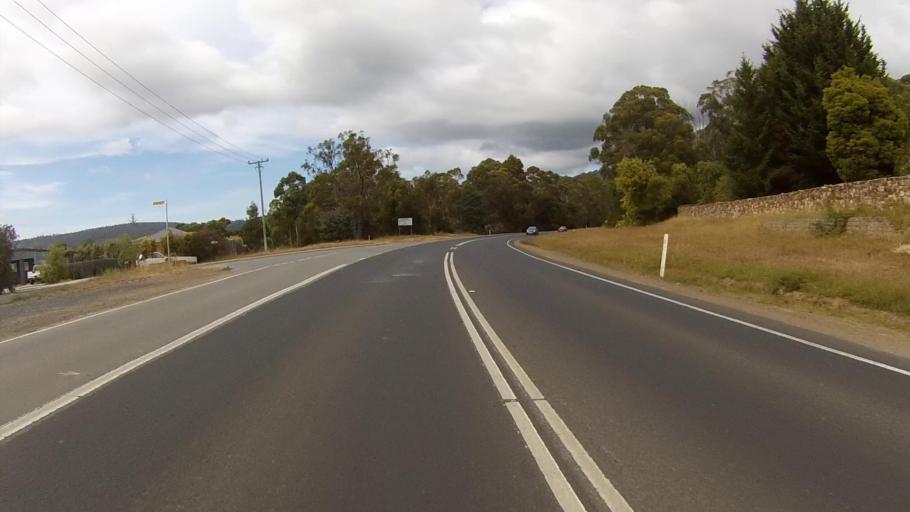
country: AU
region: Tasmania
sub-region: Kingborough
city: Margate
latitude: -43.0535
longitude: 147.2627
